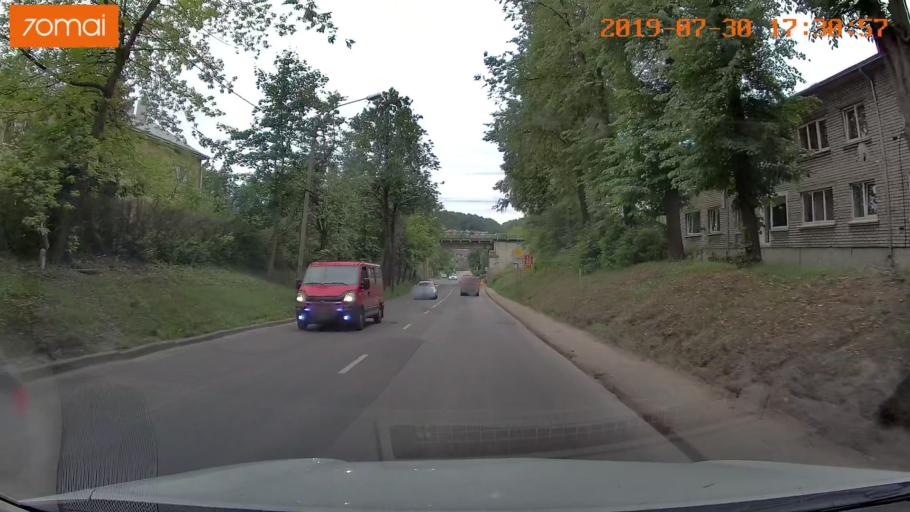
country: LT
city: Skaidiskes
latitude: 54.6939
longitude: 25.3969
